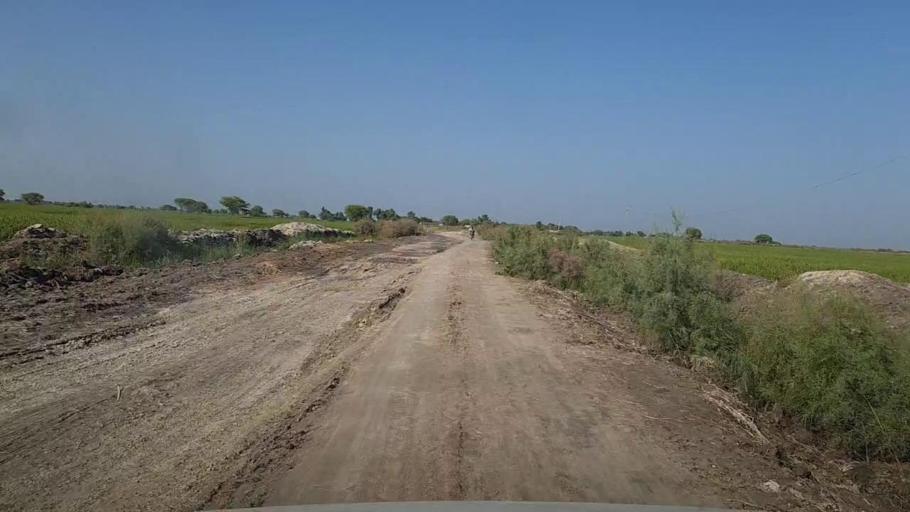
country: PK
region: Sindh
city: Kandhkot
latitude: 28.2761
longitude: 69.3163
